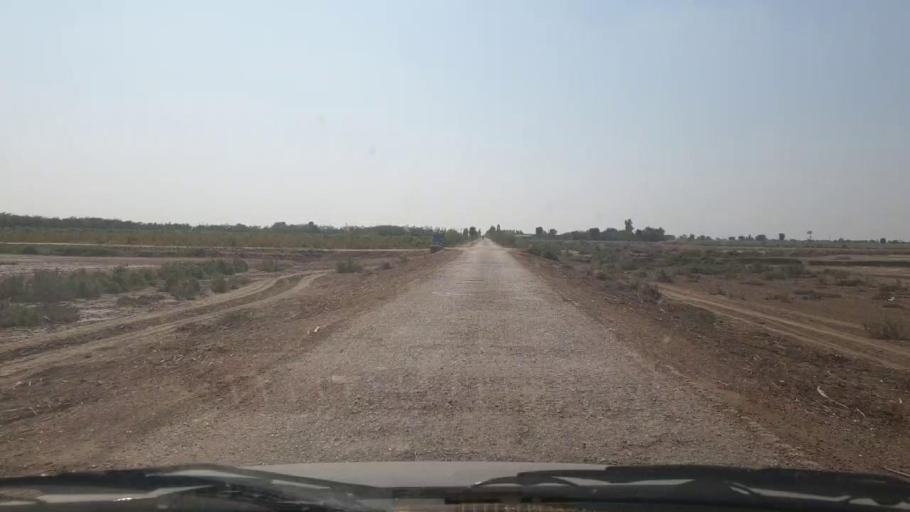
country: PK
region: Sindh
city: Samaro
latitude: 25.2359
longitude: 69.3390
